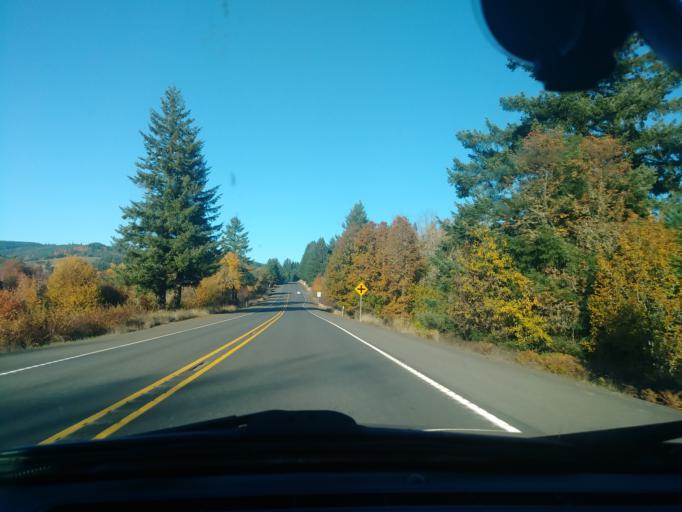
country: US
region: Oregon
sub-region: Washington County
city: Banks
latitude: 45.6114
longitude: -123.2297
